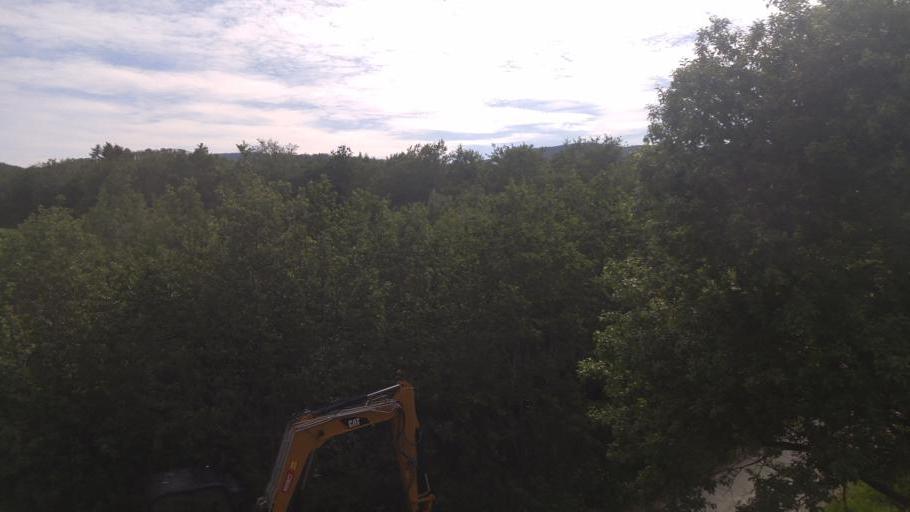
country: NO
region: Sor-Trondelag
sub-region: Melhus
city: Lundamo
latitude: 63.1837
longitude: 10.3085
